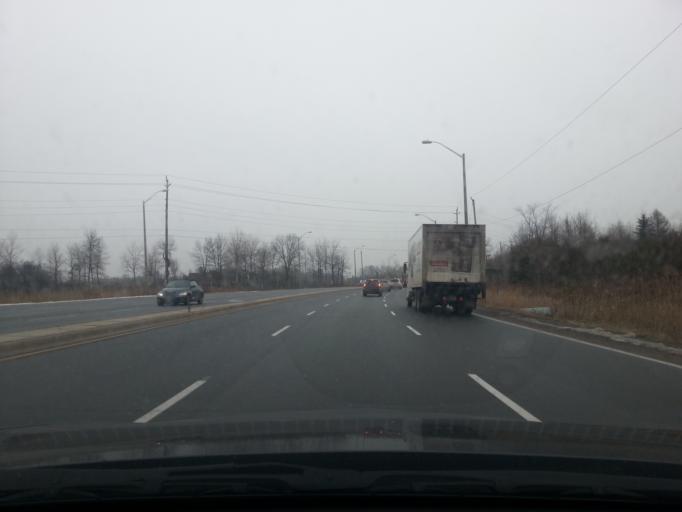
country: CA
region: Ontario
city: Peterborough
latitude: 44.2676
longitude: -78.3469
